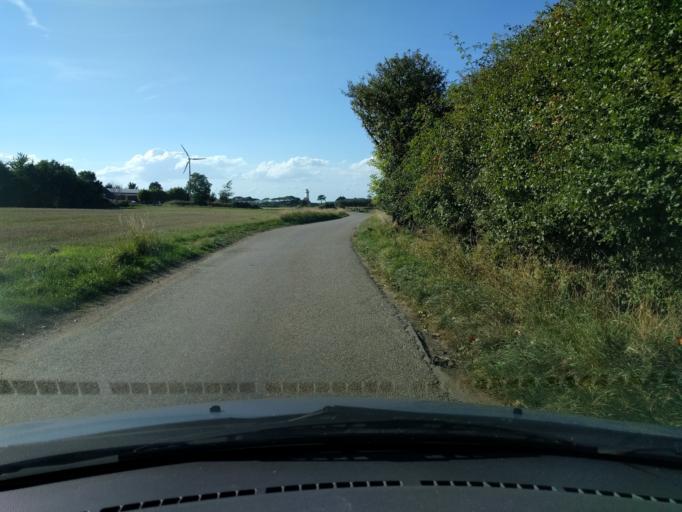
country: DK
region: South Denmark
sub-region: Assens Kommune
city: Harby
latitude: 55.1333
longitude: 9.9914
